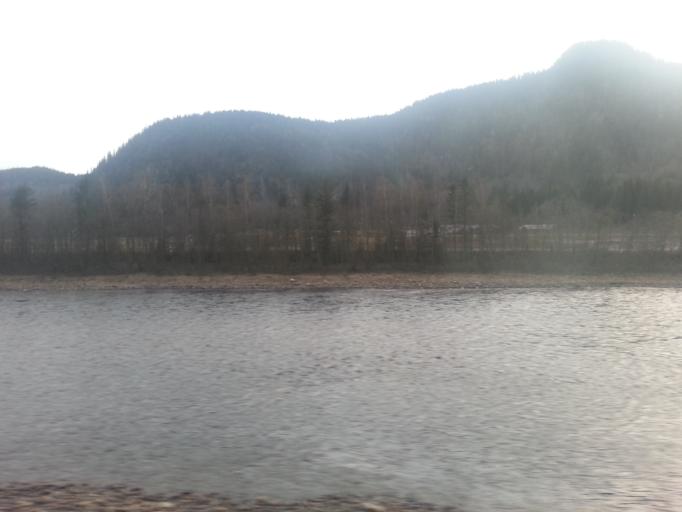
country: NO
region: Sor-Trondelag
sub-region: Midtre Gauldal
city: Storen
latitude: 63.0699
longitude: 10.2620
